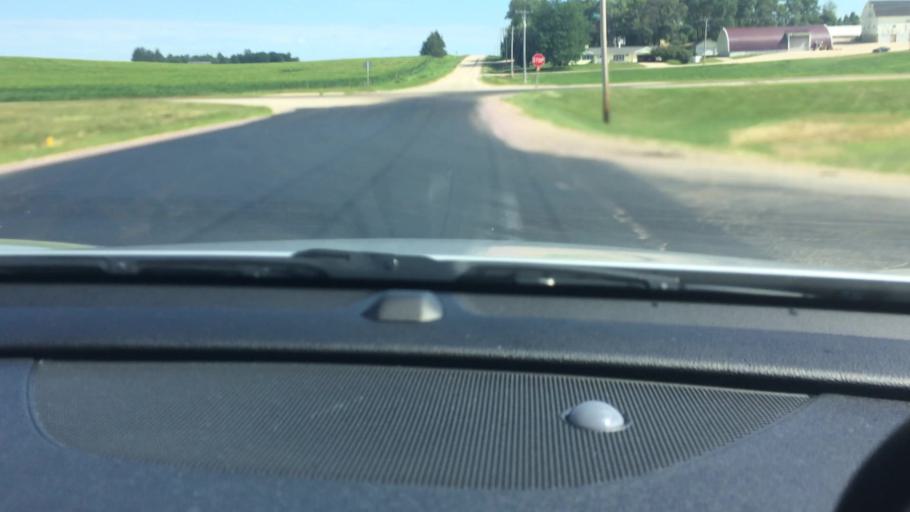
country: US
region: Wisconsin
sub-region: Columbia County
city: Lodi
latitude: 43.3315
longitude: -89.4625
